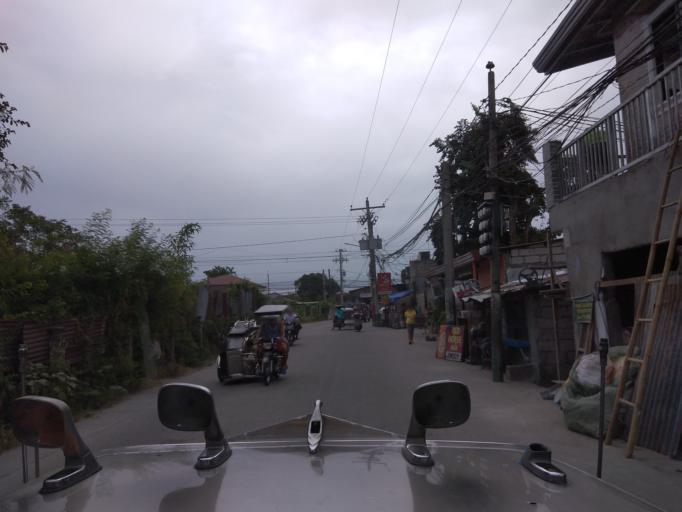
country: PH
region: Central Luzon
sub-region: Province of Pampanga
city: Mexico
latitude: 15.0614
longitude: 120.7189
